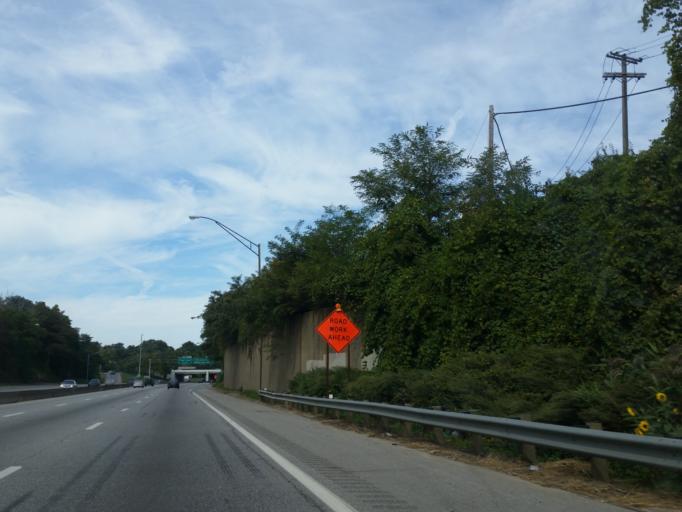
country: US
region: Ohio
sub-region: Cuyahoga County
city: Newburgh Heights
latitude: 41.4446
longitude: -81.6527
